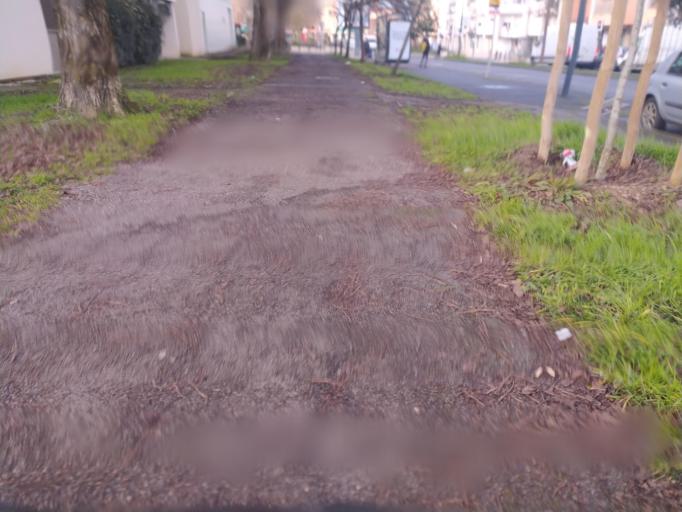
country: FR
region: Midi-Pyrenees
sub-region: Departement de la Haute-Garonne
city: Blagnac
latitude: 43.5812
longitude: 1.3895
